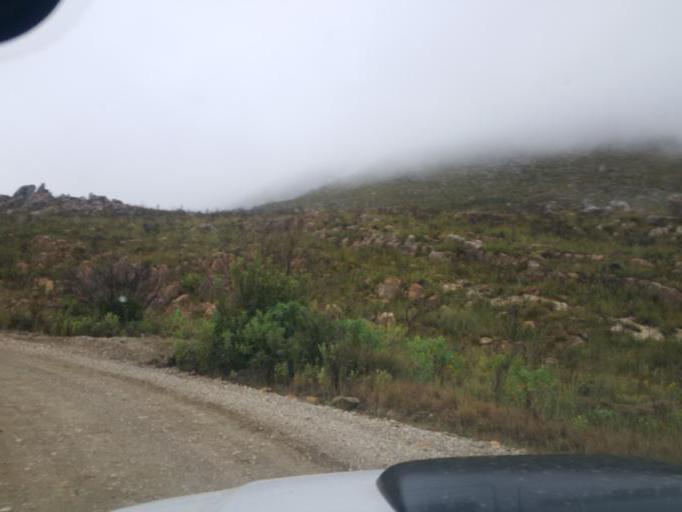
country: ZA
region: Western Cape
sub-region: Central Karoo District Municipality
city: Prince Albert
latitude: -33.3613
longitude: 22.0863
